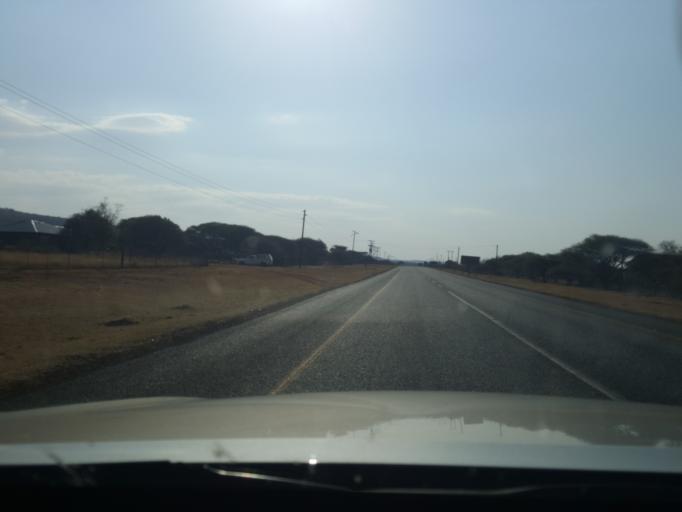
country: BW
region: South East
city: Lobatse
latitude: -25.4311
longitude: 25.8341
